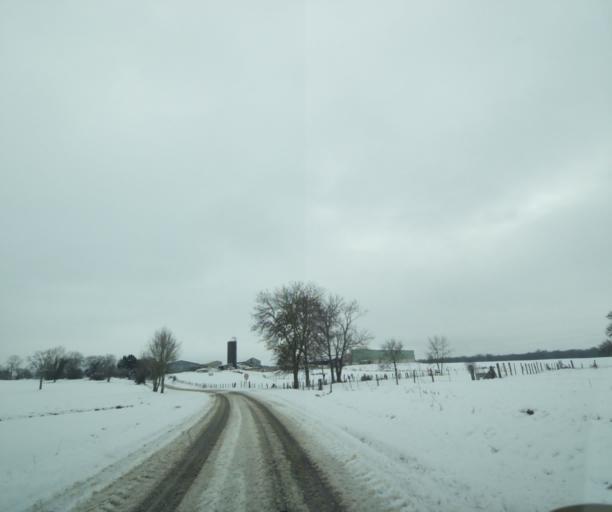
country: FR
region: Champagne-Ardenne
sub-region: Departement de la Haute-Marne
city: Montier-en-Der
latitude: 48.5127
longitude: 4.6877
